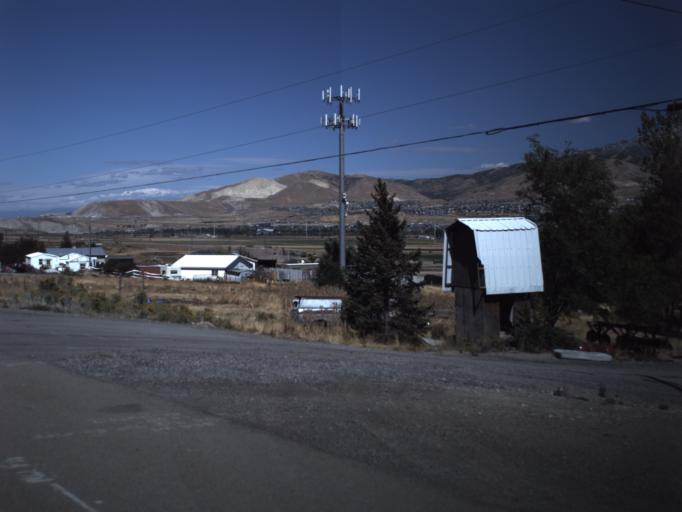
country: US
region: Utah
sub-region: Utah County
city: Saratoga Springs
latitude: 40.4059
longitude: -111.9210
